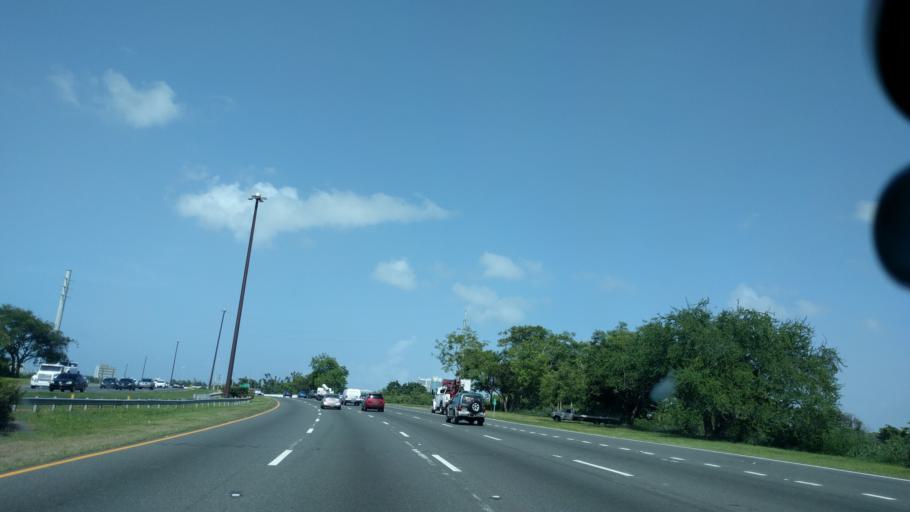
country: PR
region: Catano
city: Catano
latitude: 18.4202
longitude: -66.0838
